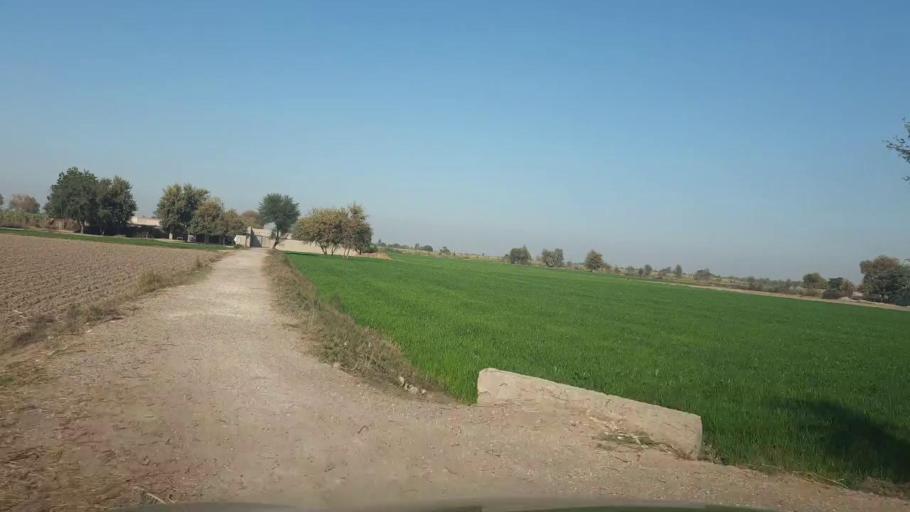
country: PK
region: Sindh
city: Mirpur Mathelo
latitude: 27.9973
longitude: 69.4856
